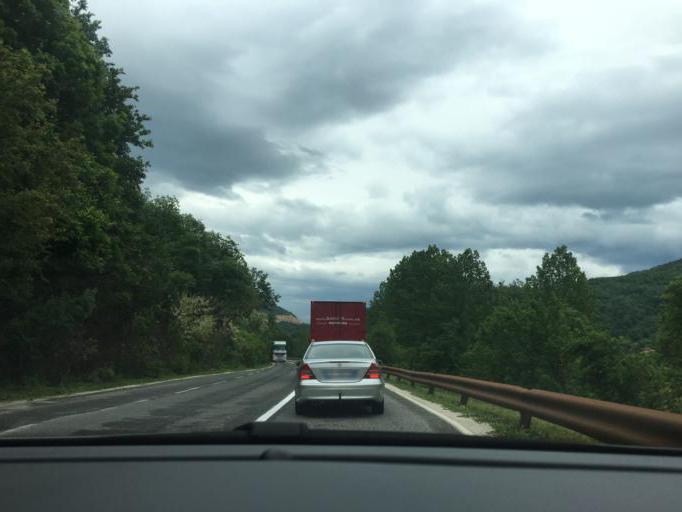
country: MK
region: Drugovo
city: Drugovo
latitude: 41.4776
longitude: 20.8799
